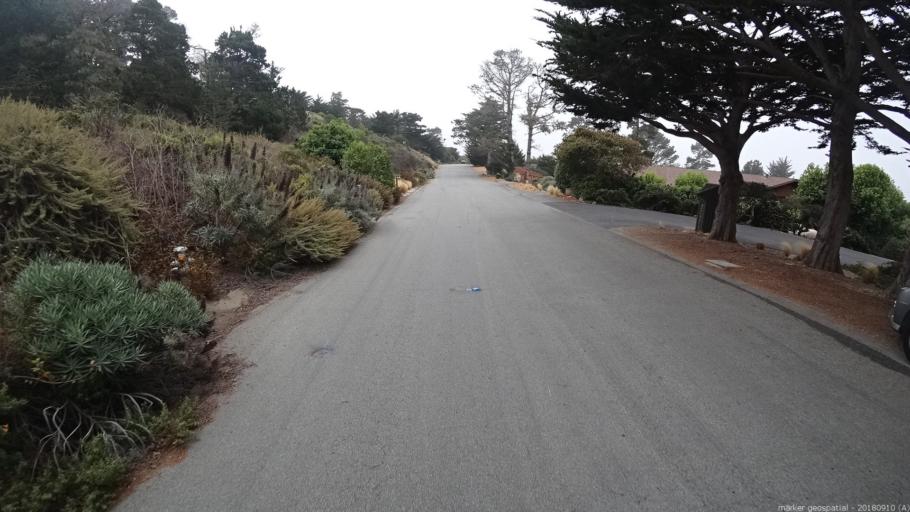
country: US
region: California
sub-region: Monterey County
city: Carmel-by-the-Sea
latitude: 36.4863
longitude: -121.9367
